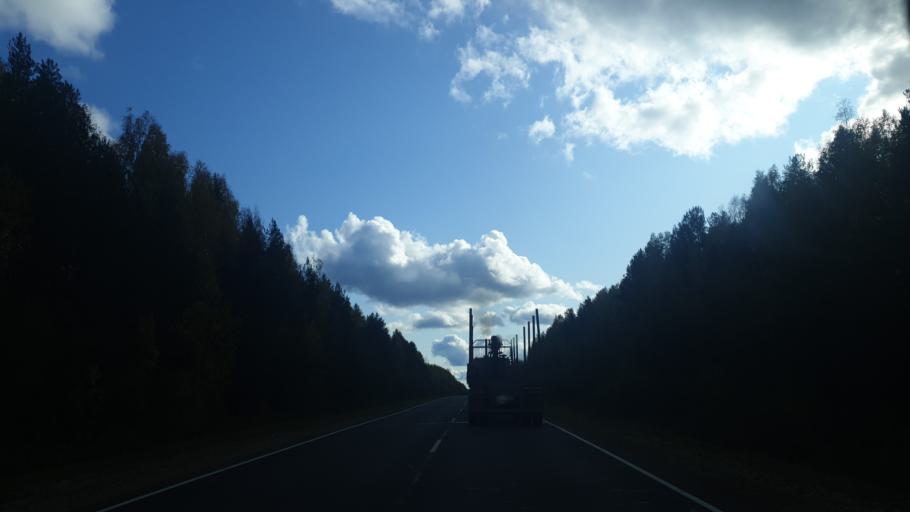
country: RU
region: Komi Republic
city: Vizinga
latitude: 60.4465
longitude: 49.6802
